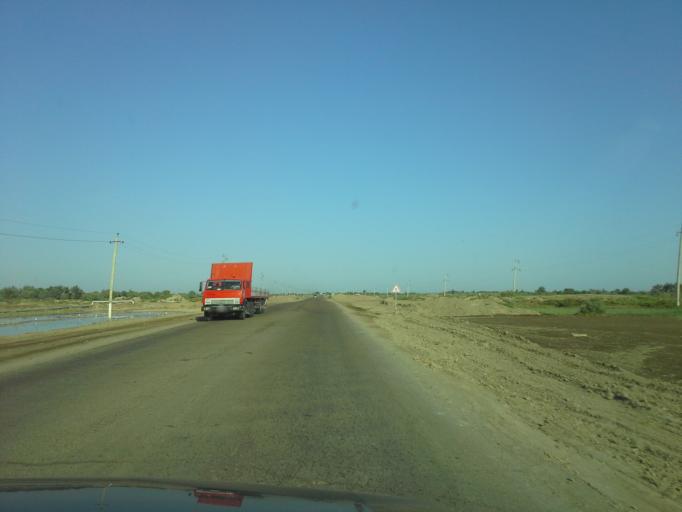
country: UZ
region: Karakalpakstan
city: Khujayli
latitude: 42.2220
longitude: 59.4864
